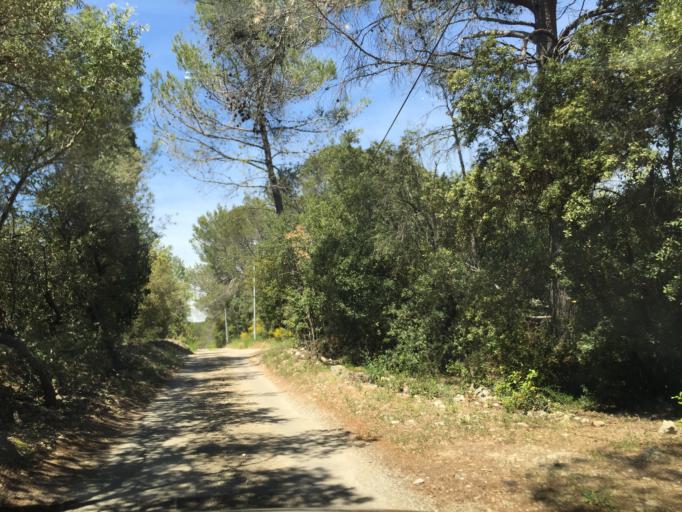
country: FR
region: Provence-Alpes-Cote d'Azur
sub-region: Departement du Var
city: Lorgues
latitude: 43.4729
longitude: 6.3709
